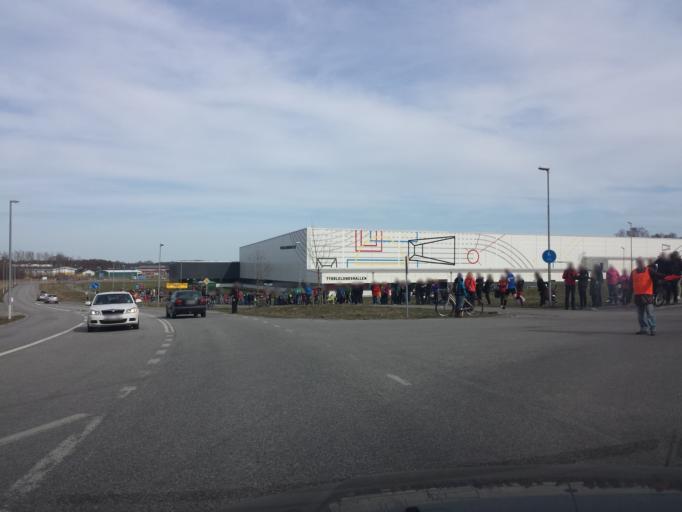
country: SE
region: OErebro
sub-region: Orebro Kommun
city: Orebro
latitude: 59.2563
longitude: 15.2576
